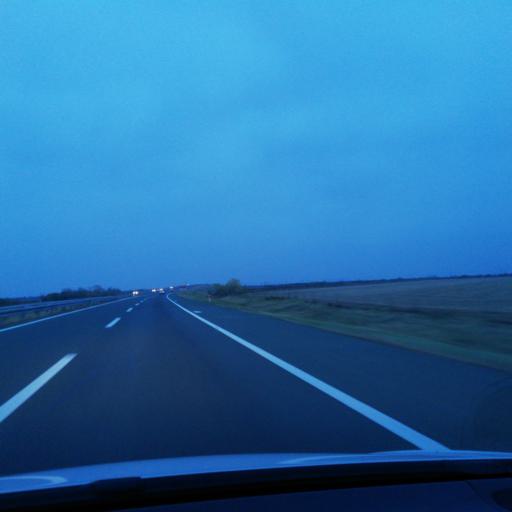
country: RS
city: Sasinci
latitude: 44.9938
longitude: 19.7001
